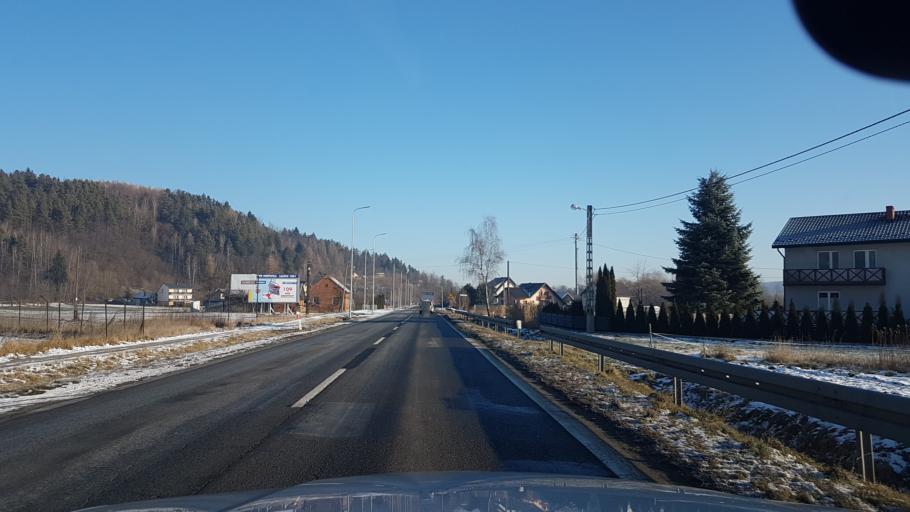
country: PL
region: Lesser Poland Voivodeship
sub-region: Powiat nowosadecki
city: Olszana
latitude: 49.5393
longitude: 20.5539
